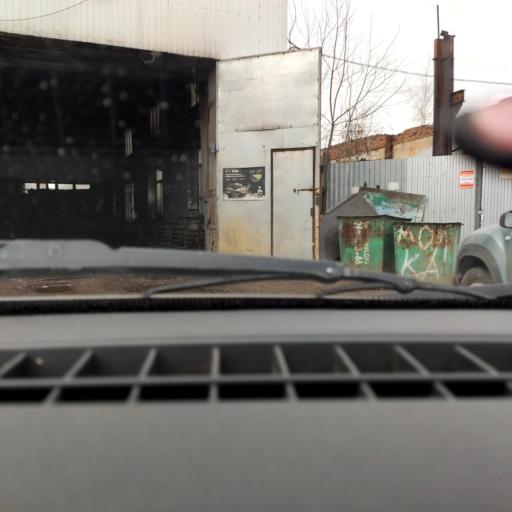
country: RU
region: Bashkortostan
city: Ufa
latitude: 54.7971
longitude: 56.1363
